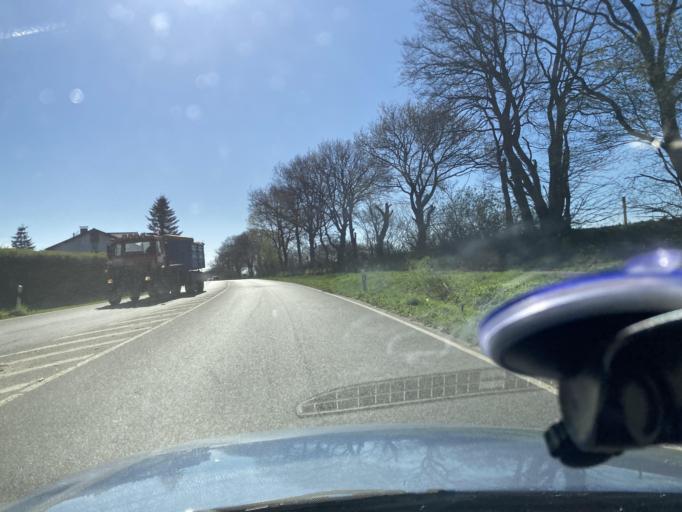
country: DE
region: Schleswig-Holstein
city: Ostrohe
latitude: 54.1967
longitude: 9.1426
